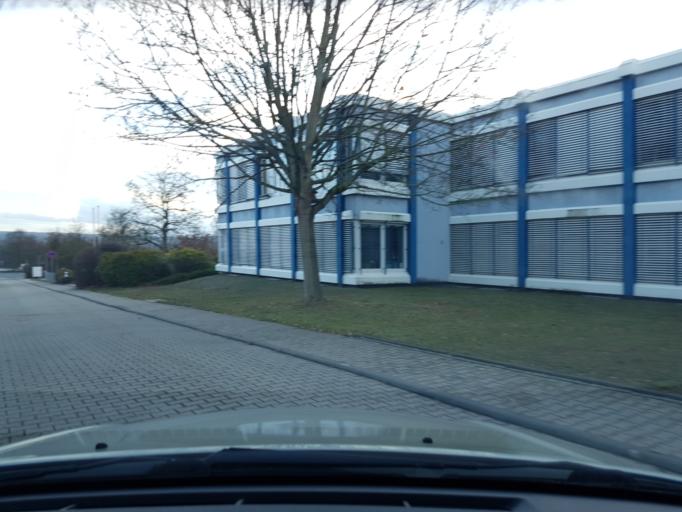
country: DE
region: Hesse
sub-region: Regierungsbezirk Darmstadt
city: Eltville
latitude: 50.0238
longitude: 8.1091
